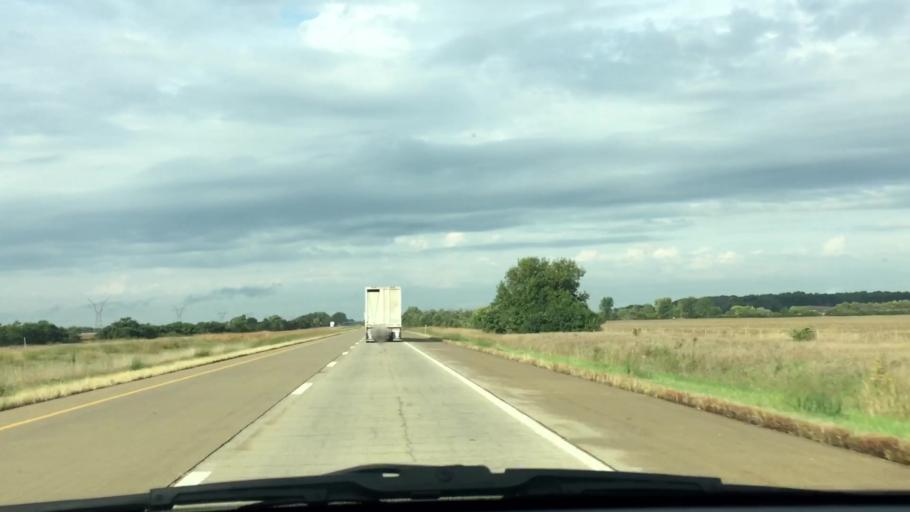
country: US
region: Illinois
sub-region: Whiteside County
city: Sterling
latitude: 41.7656
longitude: -89.8063
